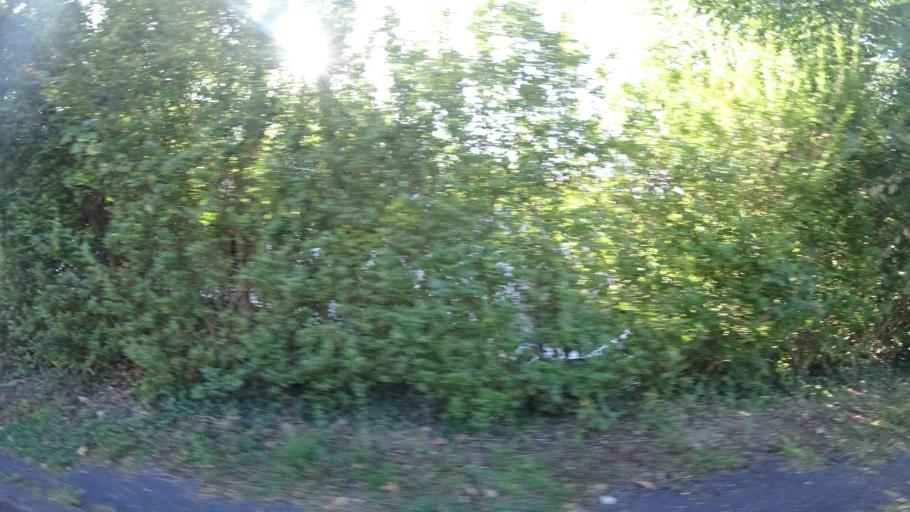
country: FR
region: Midi-Pyrenees
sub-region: Departement de l'Aveyron
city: Cransac
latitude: 44.5267
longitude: 2.2795
